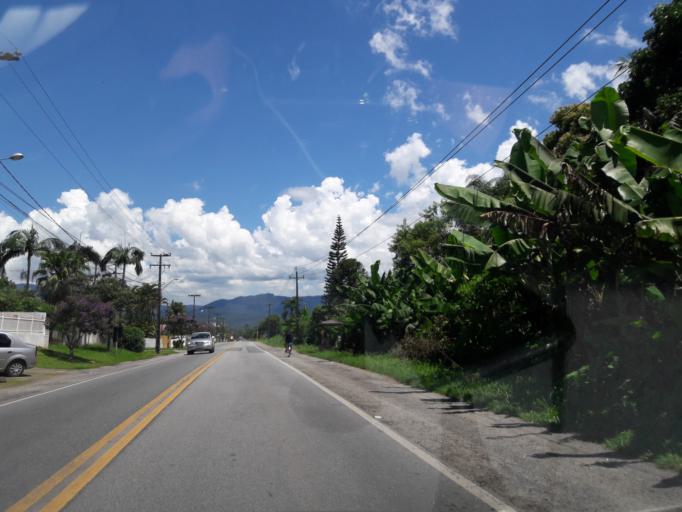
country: BR
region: Parana
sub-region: Antonina
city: Antonina
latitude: -25.4667
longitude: -48.8266
